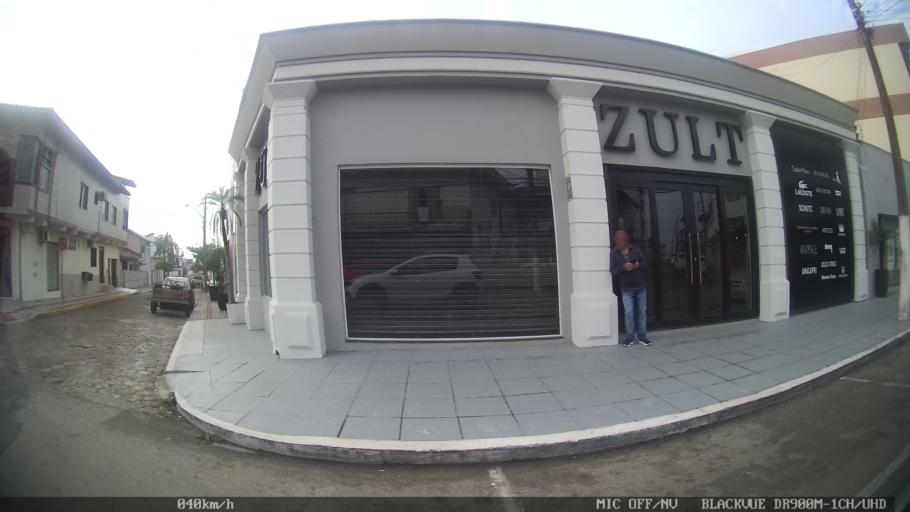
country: BR
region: Santa Catarina
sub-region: Barra Velha
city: Barra Velha
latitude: -26.6433
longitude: -48.6849
